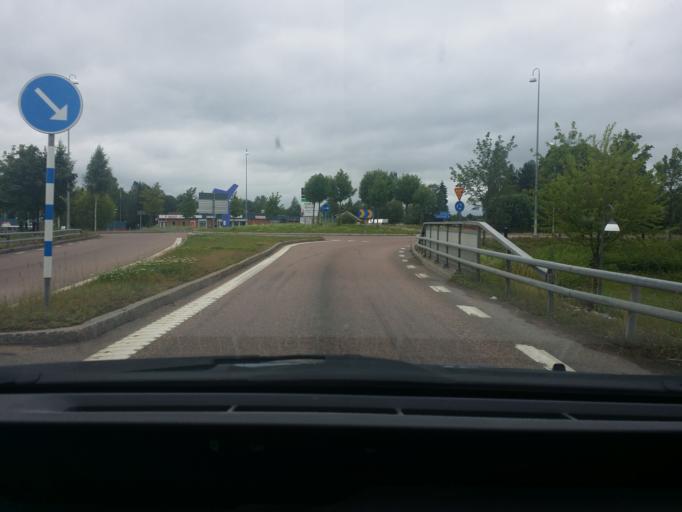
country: SE
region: Dalarna
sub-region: Gagnefs Kommun
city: Djuras
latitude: 60.5604
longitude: 15.1340
